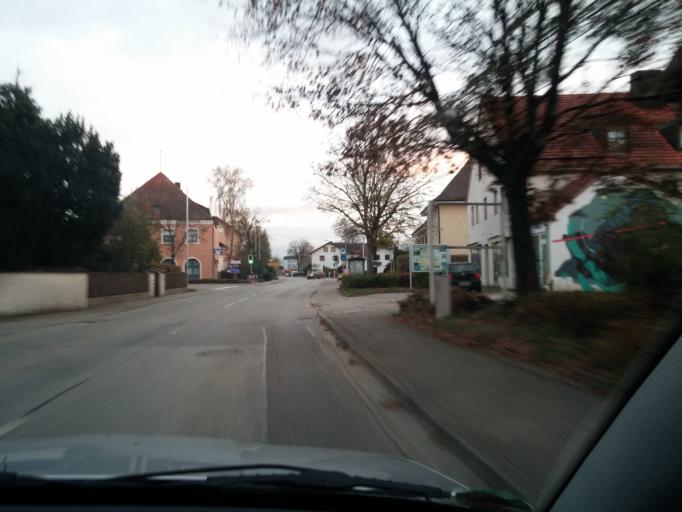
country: DE
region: Bavaria
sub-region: Upper Bavaria
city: Forstern
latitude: 48.1845
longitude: 11.9769
